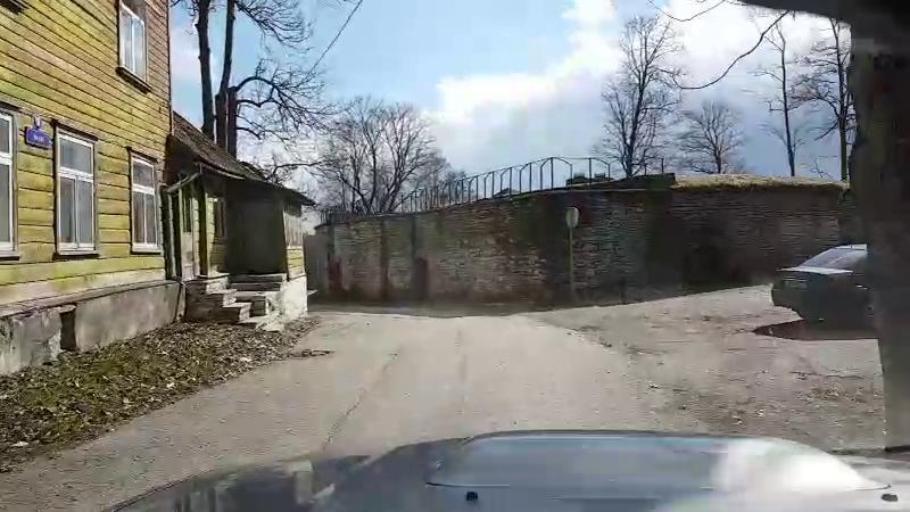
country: EE
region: Jaervamaa
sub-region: Paide linn
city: Paide
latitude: 58.8903
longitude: 25.5731
